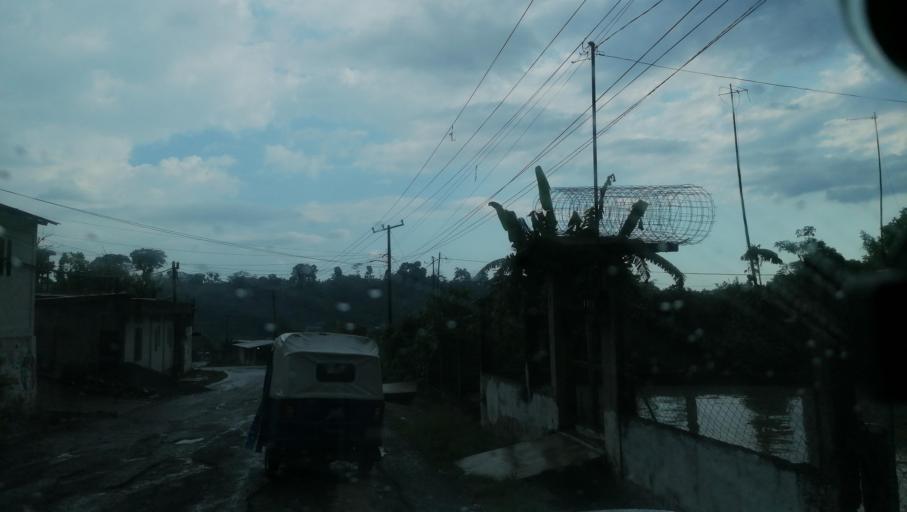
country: MX
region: Chiapas
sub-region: Cacahoatan
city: Benito Juarez
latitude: 15.0525
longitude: -92.1898
